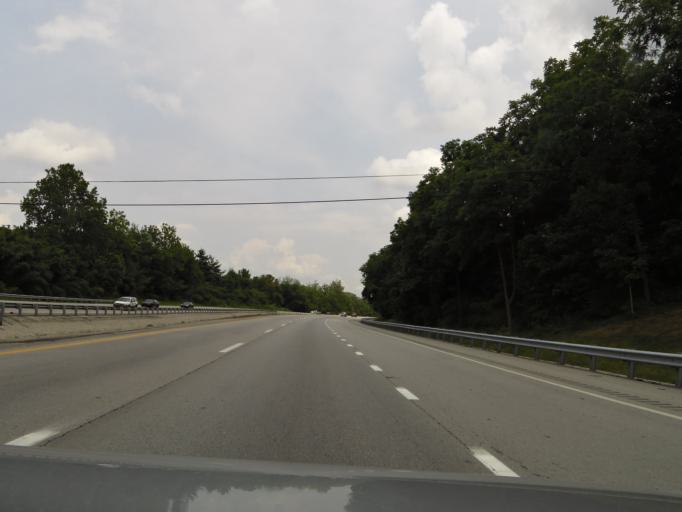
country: US
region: Kentucky
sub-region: Jefferson County
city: Northfield
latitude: 38.2915
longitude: -85.6404
